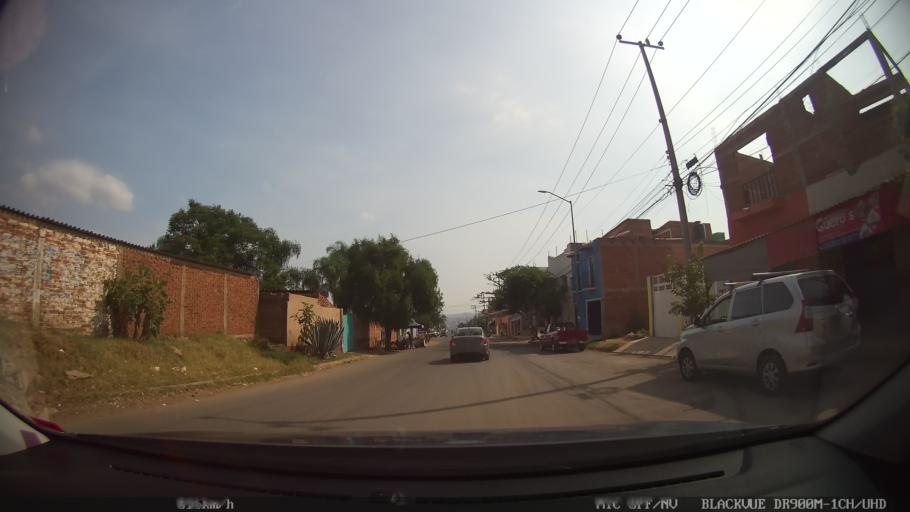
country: MX
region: Jalisco
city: Tonala
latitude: 20.6352
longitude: -103.2362
